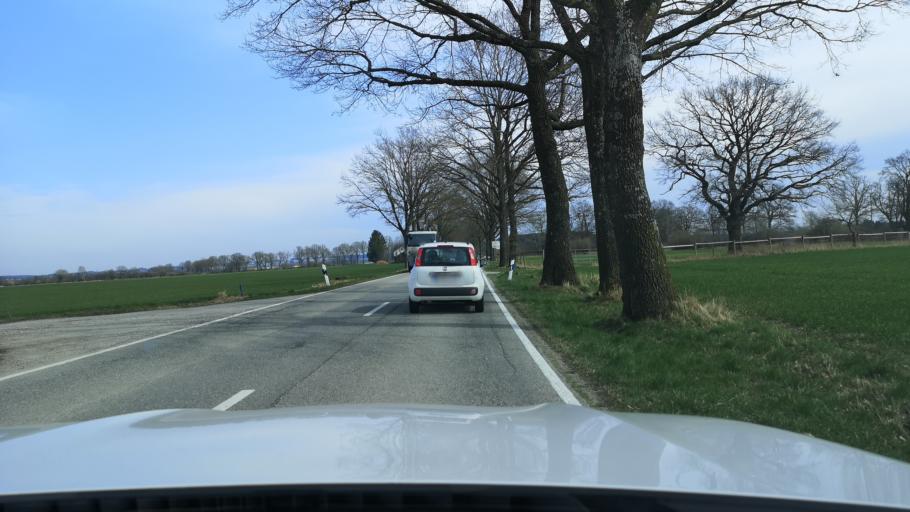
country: DE
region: Bavaria
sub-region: Upper Bavaria
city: Forstinning
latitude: 48.1968
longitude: 11.9050
